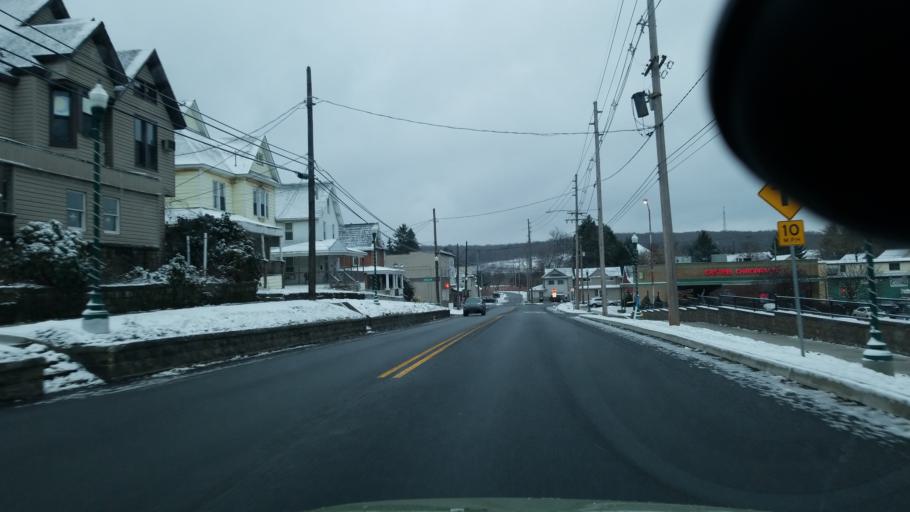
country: US
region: Pennsylvania
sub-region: Clearfield County
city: DuBois
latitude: 41.1231
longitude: -78.7675
